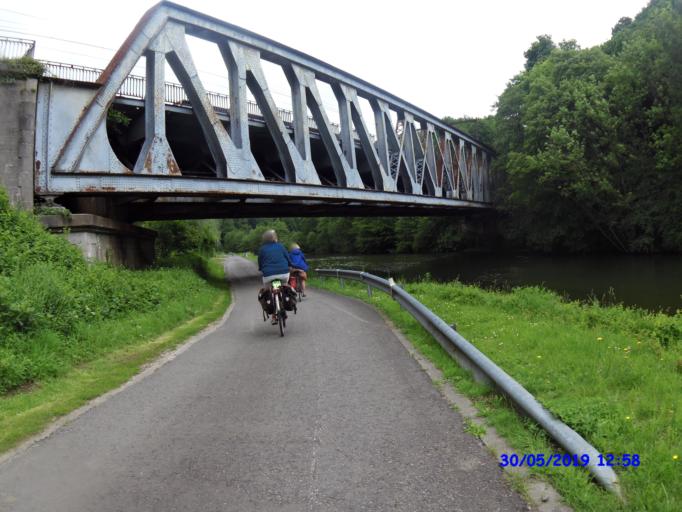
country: BE
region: Wallonia
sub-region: Province du Hainaut
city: Thuin
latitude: 50.3444
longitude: 4.2944
